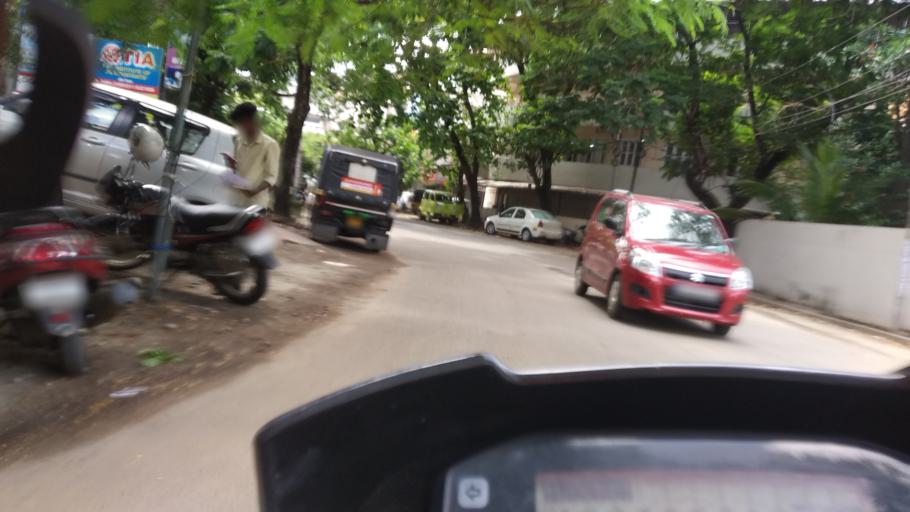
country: IN
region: Kerala
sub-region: Ernakulam
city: Cochin
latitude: 9.9913
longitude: 76.2902
